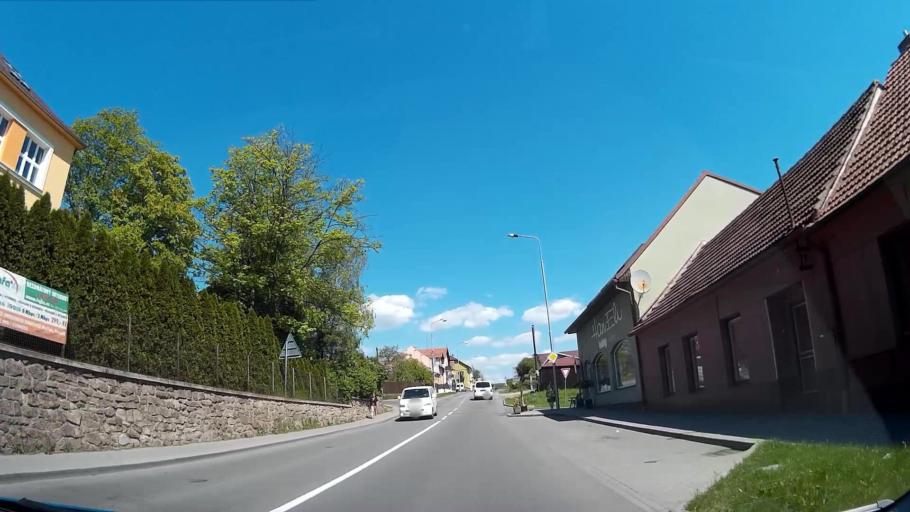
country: CZ
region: South Moravian
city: Ivancice
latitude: 49.1044
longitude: 16.3719
